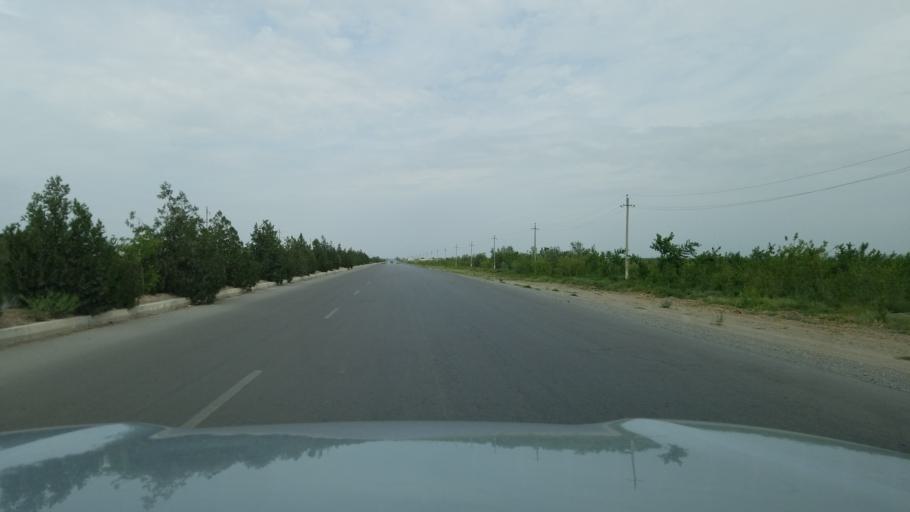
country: TM
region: Ahal
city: Arcabil
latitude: 38.2032
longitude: 57.8231
